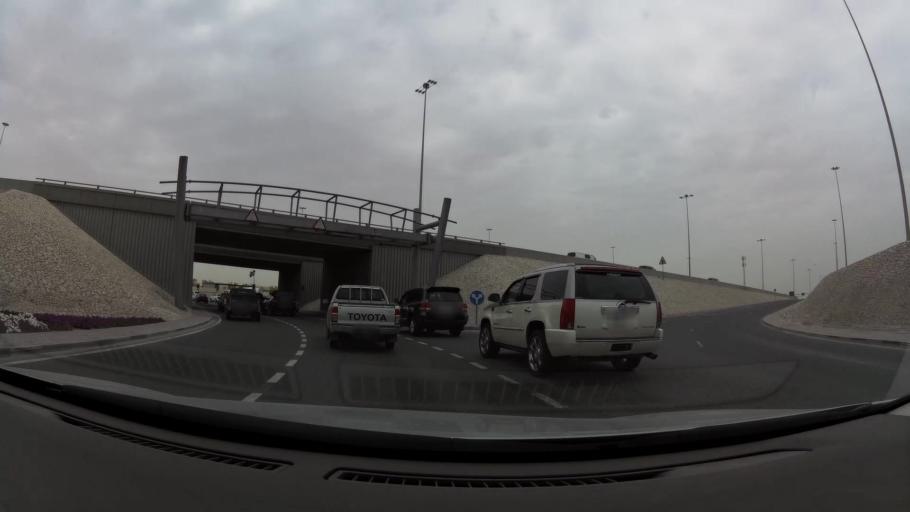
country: QA
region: Baladiyat ar Rayyan
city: Ar Rayyan
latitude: 25.3449
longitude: 51.4585
